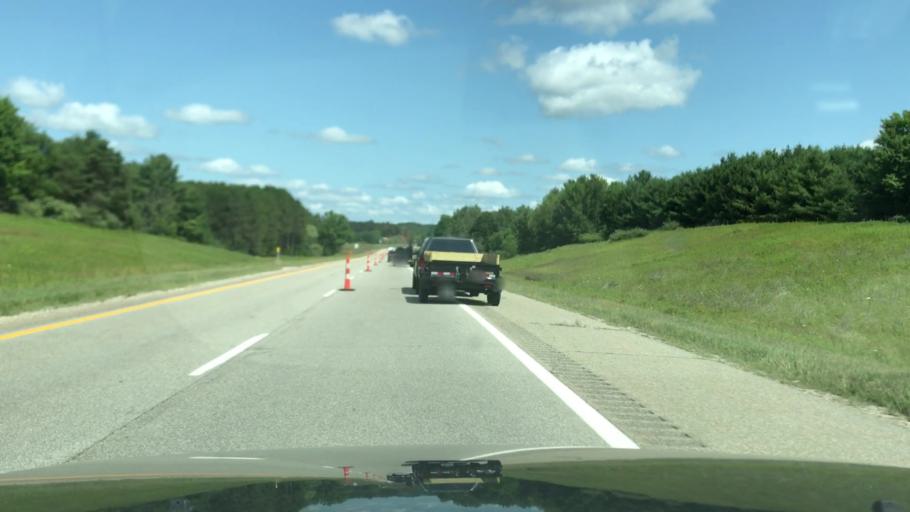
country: US
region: Michigan
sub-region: Mecosta County
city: Big Rapids
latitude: 43.7571
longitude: -85.5300
